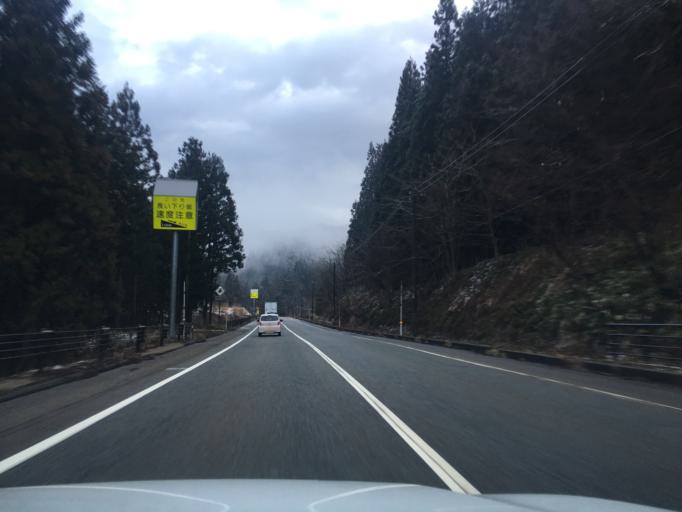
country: JP
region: Niigata
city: Murakami
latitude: 38.4136
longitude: 139.5666
